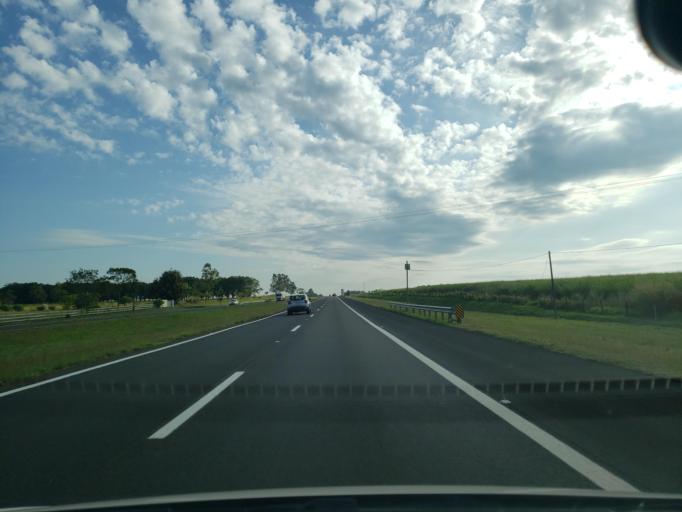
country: BR
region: Sao Paulo
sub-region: Guararapes
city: Guararapes
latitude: -21.2027
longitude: -50.6006
